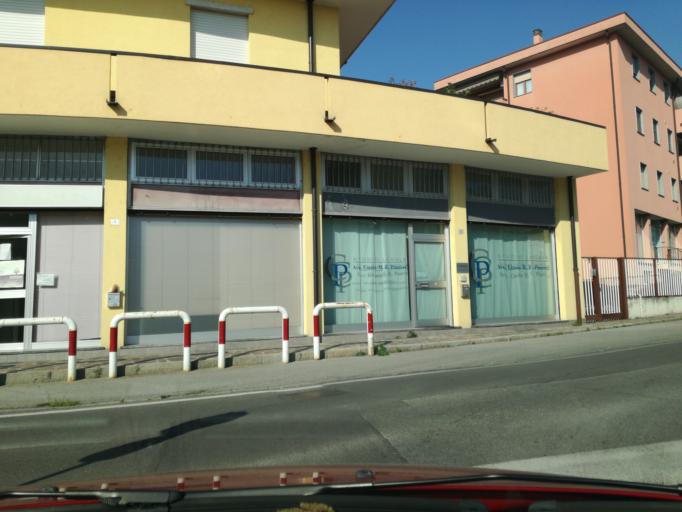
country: IT
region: Lombardy
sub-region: Provincia di Monza e Brianza
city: Cornate d'Adda
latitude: 45.6304
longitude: 9.4703
